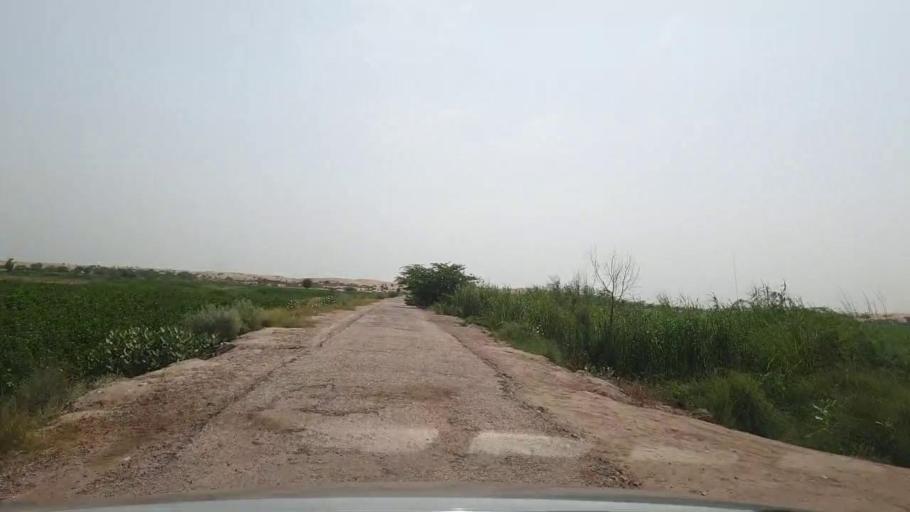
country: PK
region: Sindh
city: Rohri
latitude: 27.6181
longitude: 69.1082
